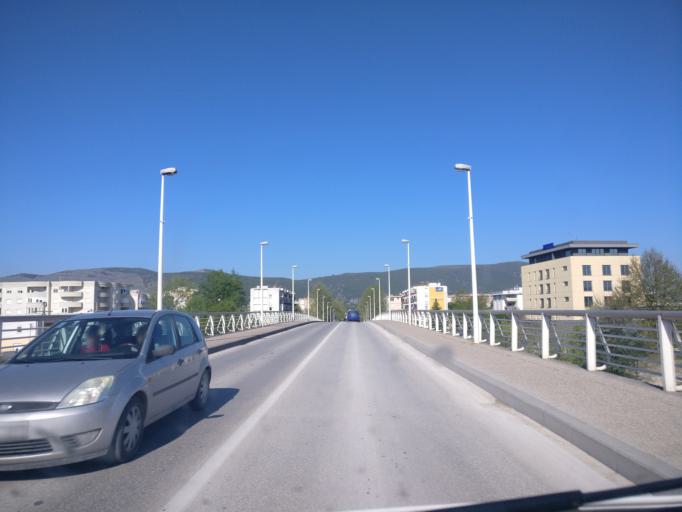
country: BA
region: Federation of Bosnia and Herzegovina
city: Tasovcici
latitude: 43.1089
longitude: 17.7073
